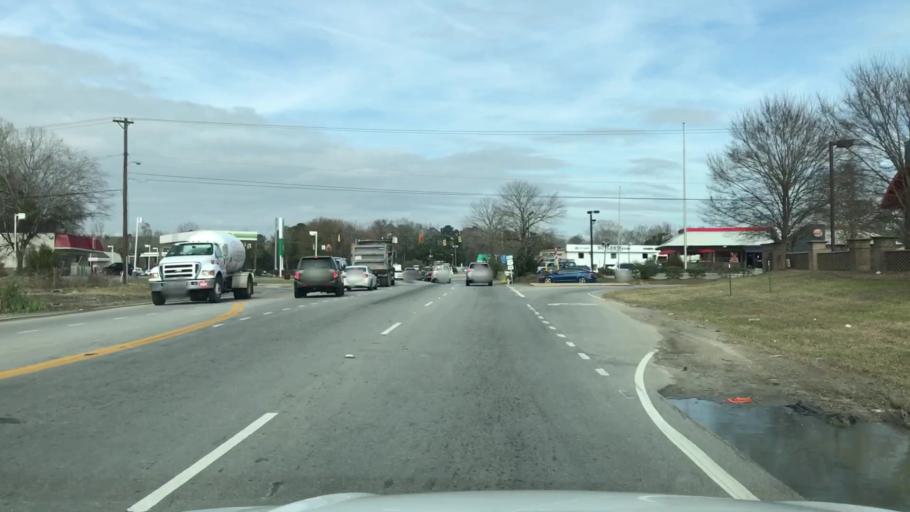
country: US
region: South Carolina
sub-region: Charleston County
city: Shell Point
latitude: 32.8012
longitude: -80.1087
